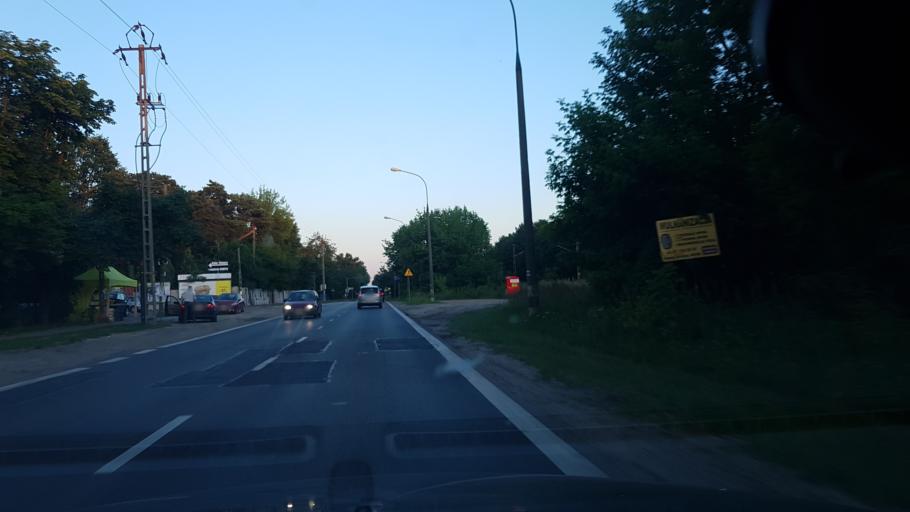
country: PL
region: Masovian Voivodeship
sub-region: Warszawa
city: Wawer
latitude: 52.1829
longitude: 21.1905
